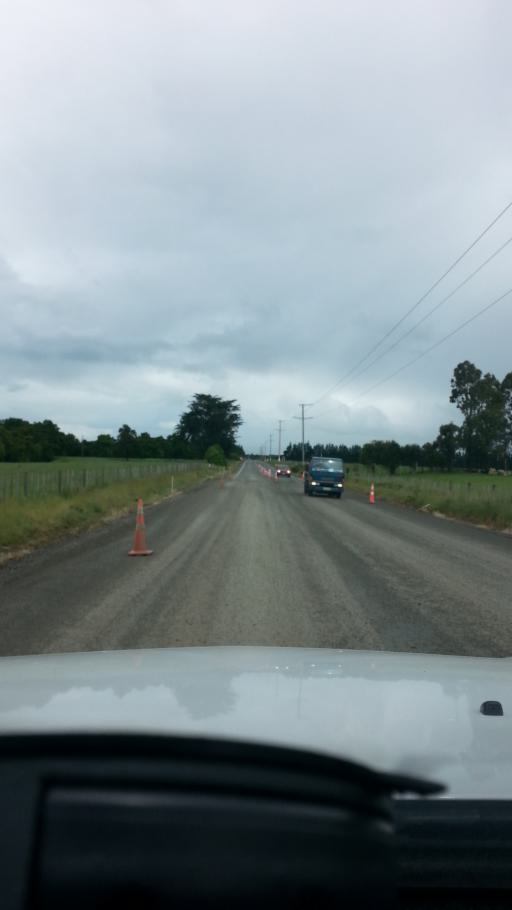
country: NZ
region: Wellington
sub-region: Masterton District
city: Masterton
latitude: -40.8341
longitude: 175.6285
